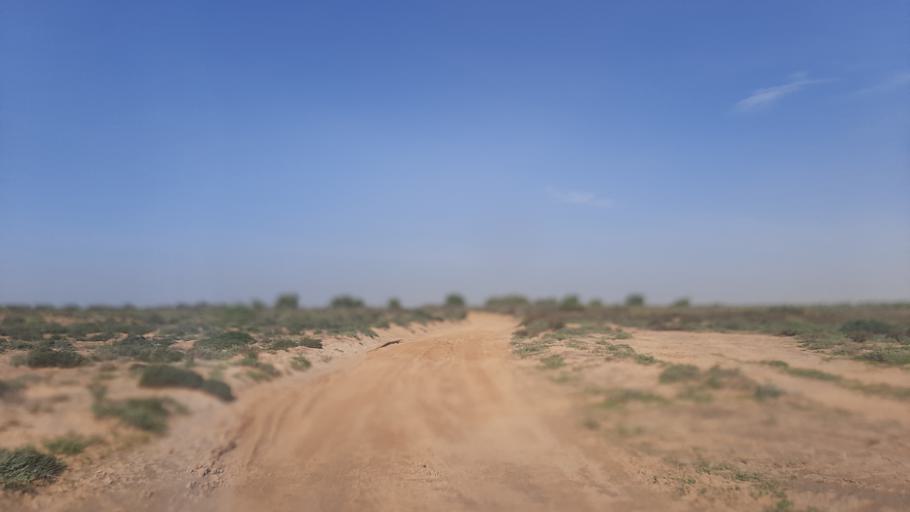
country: TN
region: Madanin
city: Zarzis
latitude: 33.4513
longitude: 10.8084
